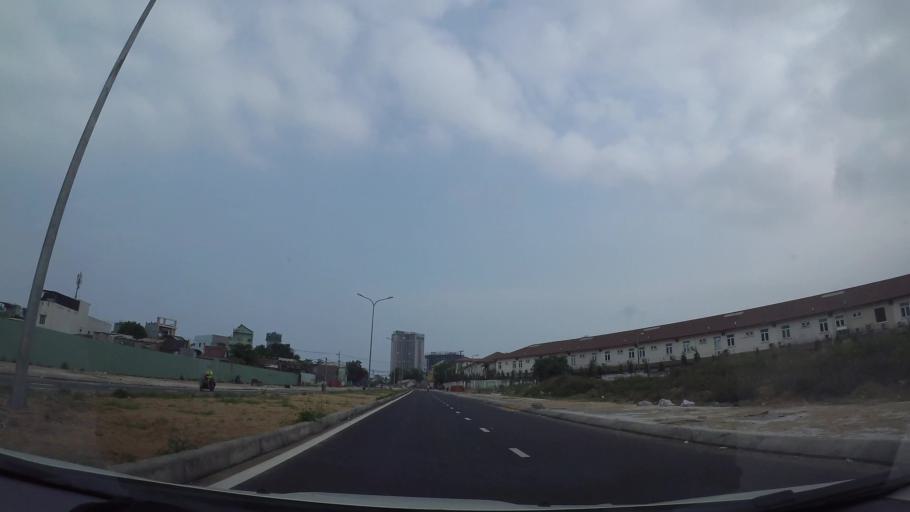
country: VN
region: Da Nang
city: Son Tra
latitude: 16.0832
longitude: 108.2386
